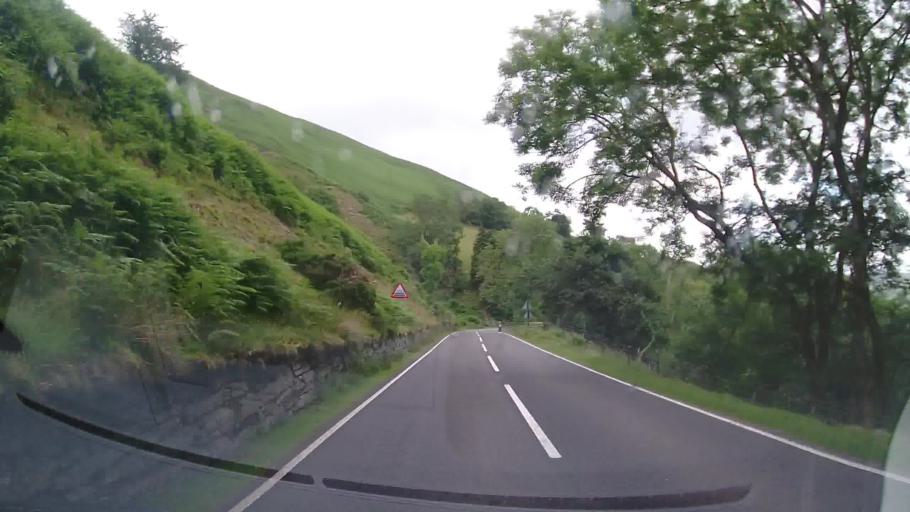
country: GB
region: Wales
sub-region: Sir Powys
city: Llangynog
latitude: 52.8512
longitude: -3.4361
